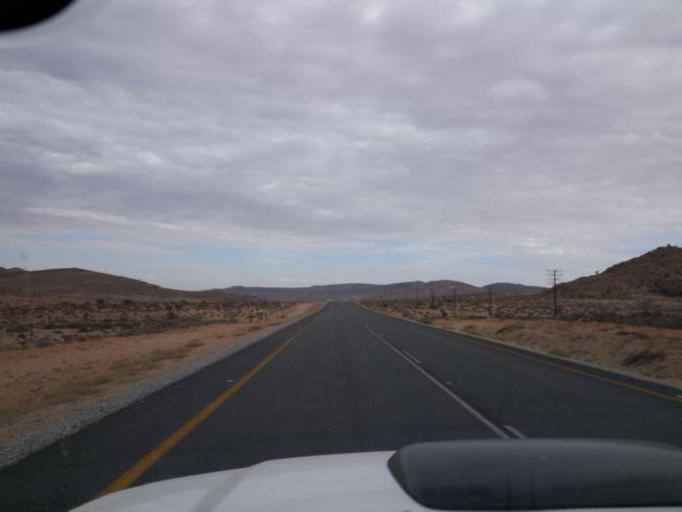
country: ZA
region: Northern Cape
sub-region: Namakwa District Municipality
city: Springbok
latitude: -29.4994
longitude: 17.8440
